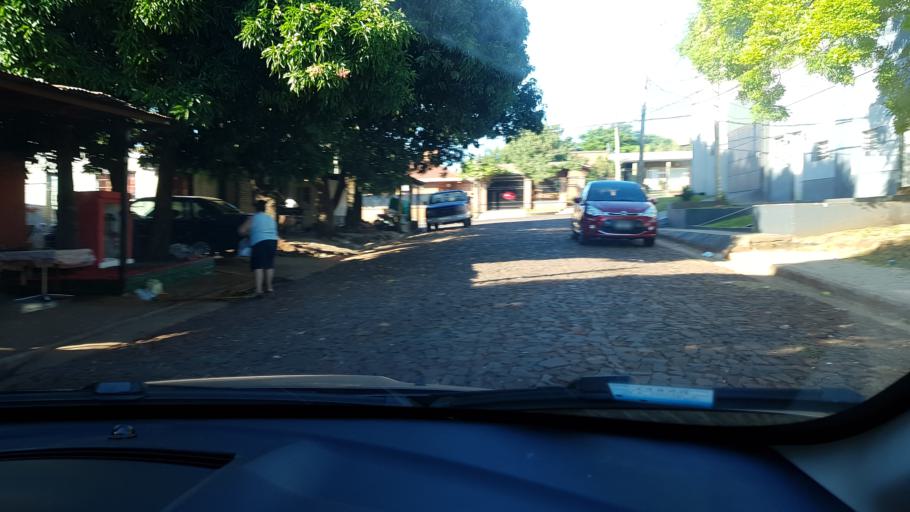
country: AR
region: Misiones
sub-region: Departamento de Capital
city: Posadas
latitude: -27.3848
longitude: -55.9128
